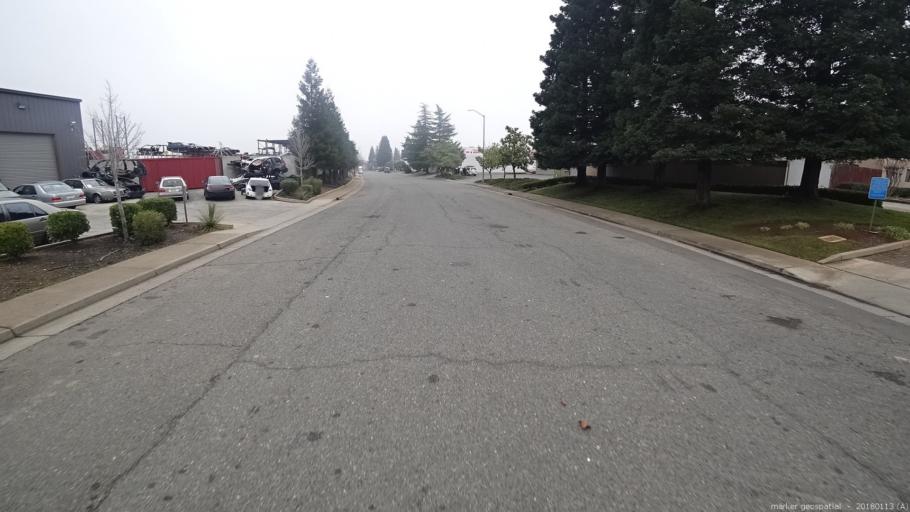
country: US
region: California
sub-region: Sacramento County
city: Rancho Cordova
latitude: 38.5691
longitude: -121.2589
